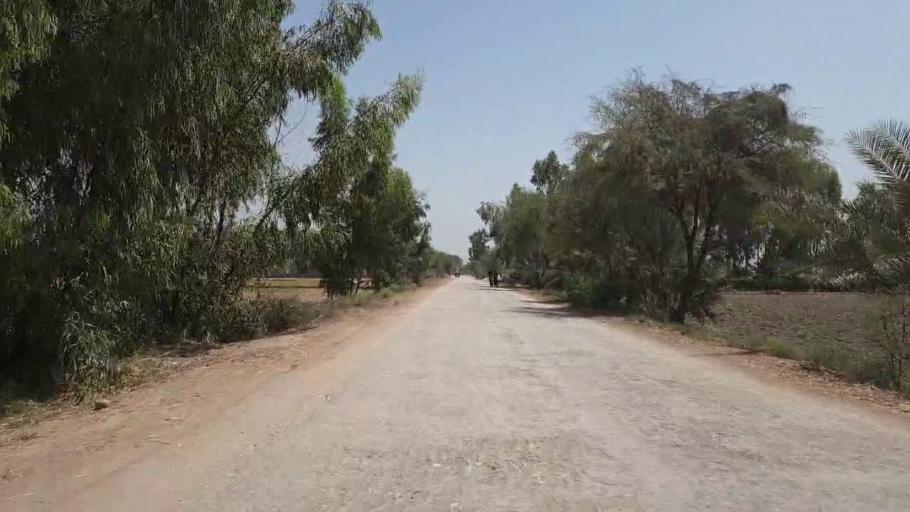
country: PK
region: Sindh
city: Adilpur
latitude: 27.8420
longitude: 69.2677
